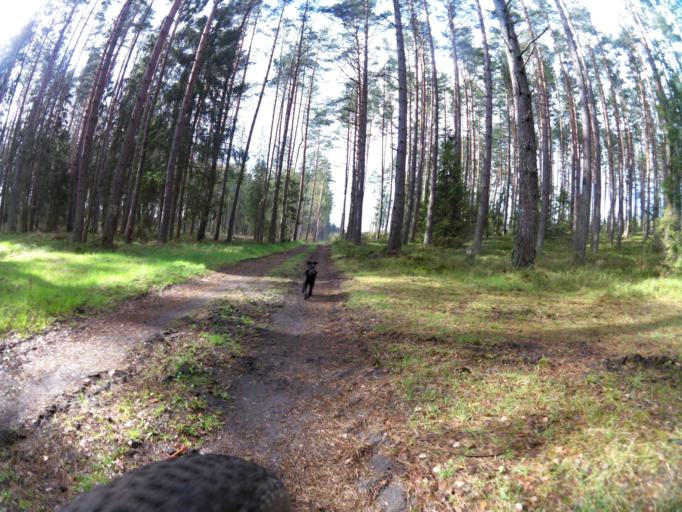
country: PL
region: Pomeranian Voivodeship
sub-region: Powiat slupski
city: Kepice
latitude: 54.2957
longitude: 16.8353
